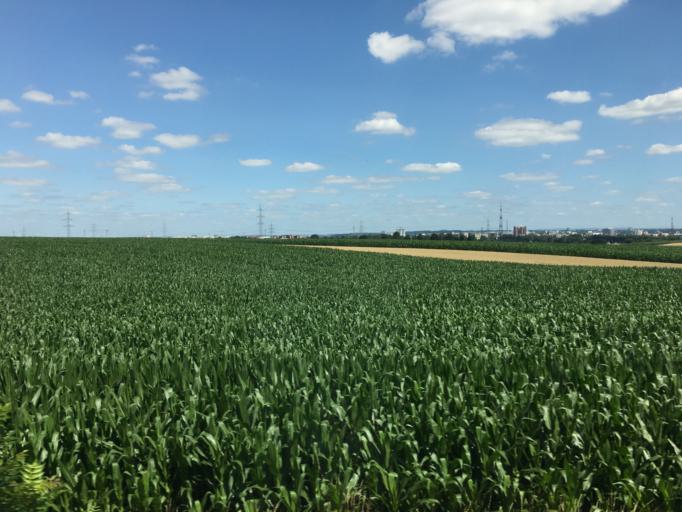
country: DE
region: Hesse
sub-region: Regierungsbezirk Darmstadt
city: Steinbach am Taunus
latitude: 50.1669
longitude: 8.5881
